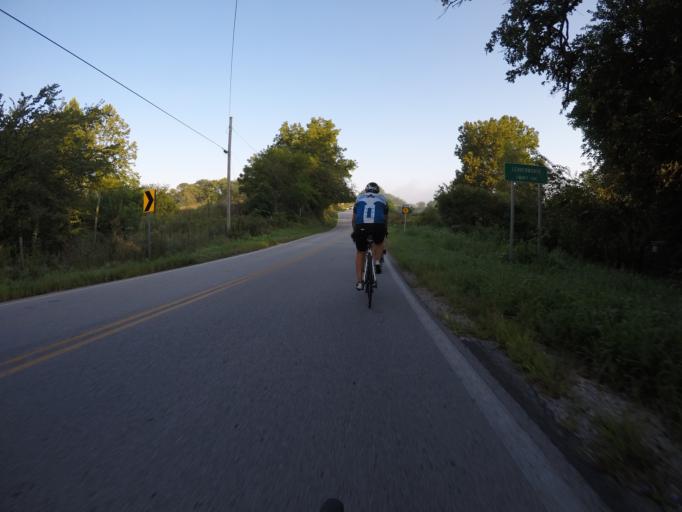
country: US
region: Kansas
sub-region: Leavenworth County
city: Lansing
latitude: 39.2020
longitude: -94.8284
